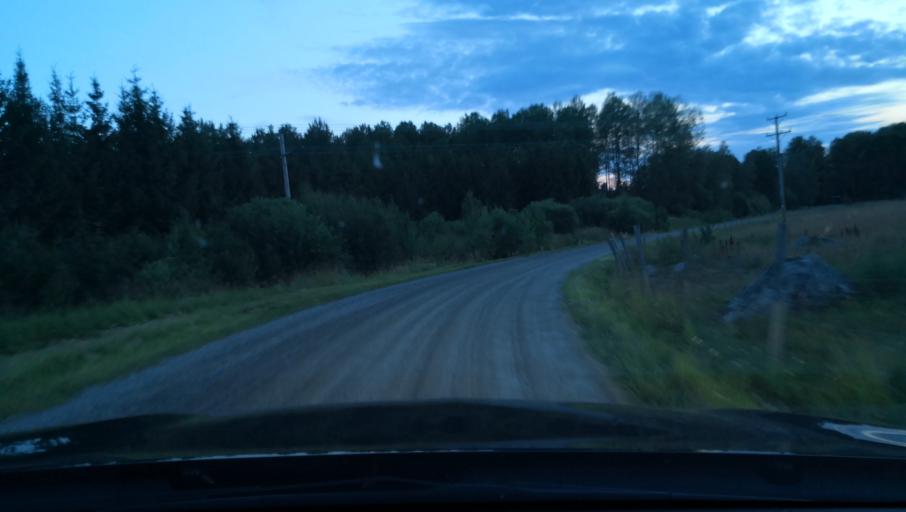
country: SE
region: Uppsala
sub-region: Heby Kommun
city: OEstervala
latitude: 60.0146
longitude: 17.2962
